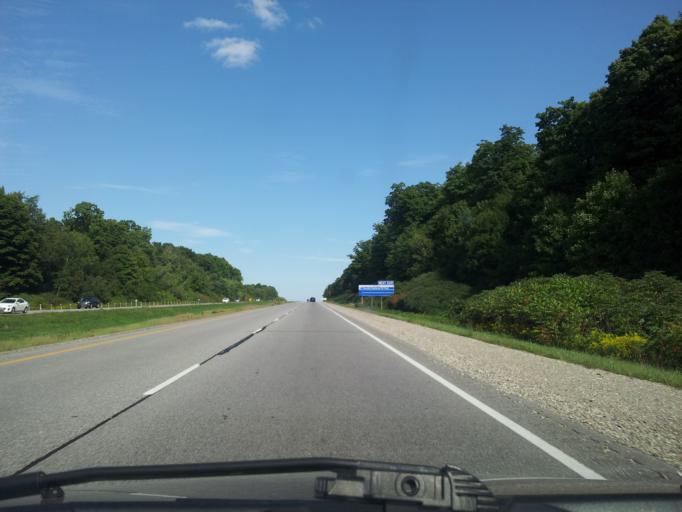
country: CA
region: Ontario
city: Kitchener
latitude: 43.3997
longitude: -80.6215
